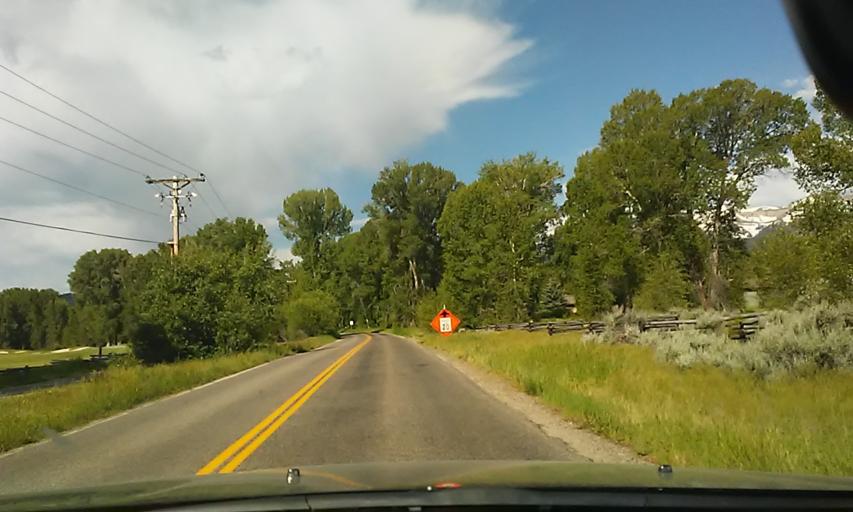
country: US
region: Wyoming
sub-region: Teton County
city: Jackson
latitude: 43.5620
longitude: -110.7561
